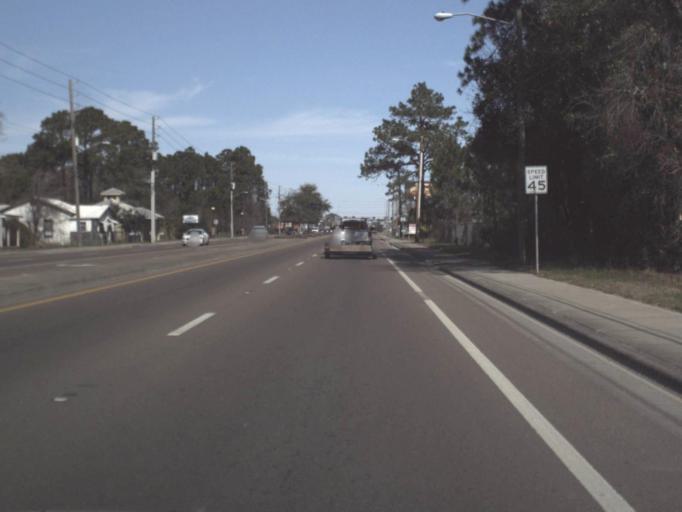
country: US
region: Florida
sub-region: Bay County
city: Panama City
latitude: 30.1789
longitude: -85.6501
